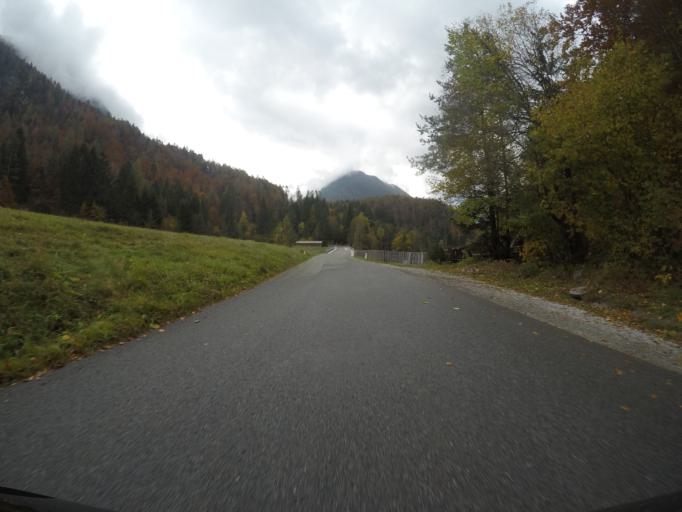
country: SI
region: Kranjska Gora
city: Mojstrana
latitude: 46.4562
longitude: 13.9394
